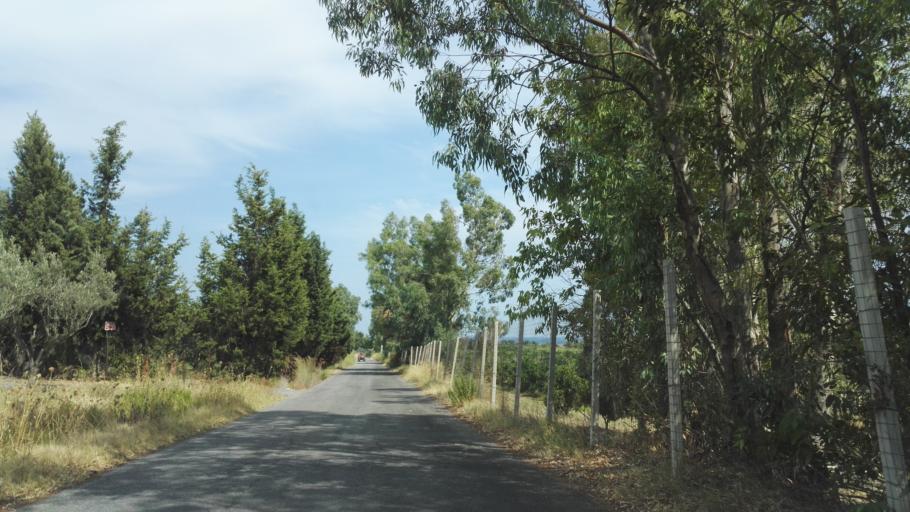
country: IT
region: Calabria
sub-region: Provincia di Reggio Calabria
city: Monasterace Marina
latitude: 38.4264
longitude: 16.5630
